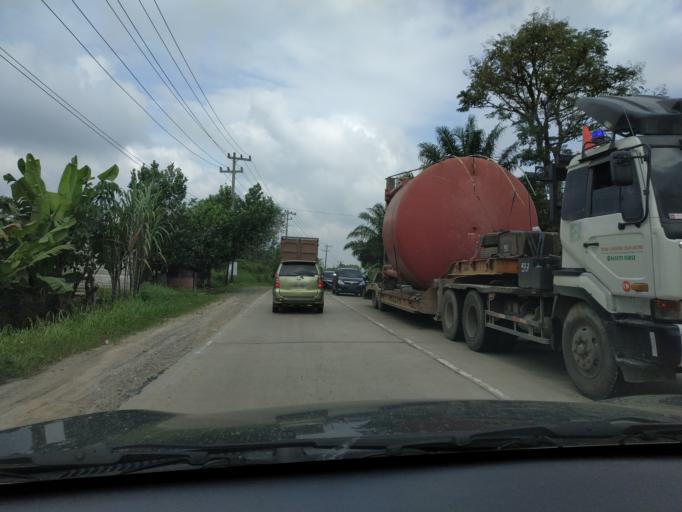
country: ID
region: Riau
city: Airmolek
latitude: -0.3842
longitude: 102.3981
